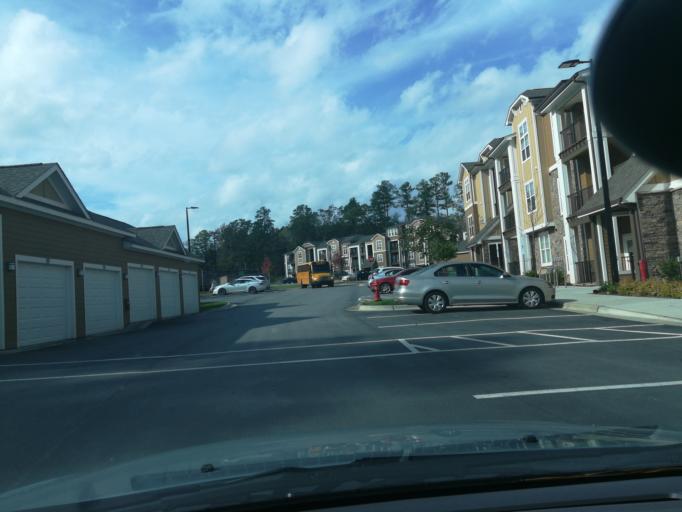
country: US
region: North Carolina
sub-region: Durham County
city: Durham
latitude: 36.0586
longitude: -78.9409
